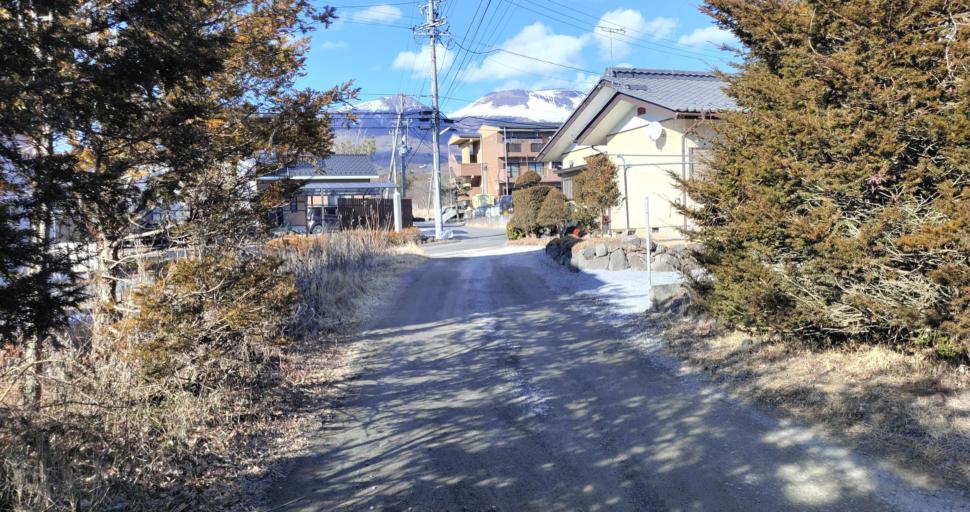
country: JP
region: Nagano
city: Komoro
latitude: 36.3318
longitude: 138.5113
